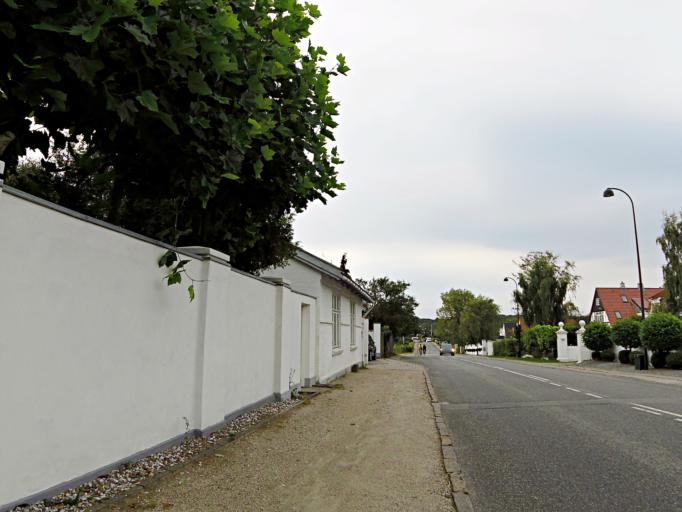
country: DK
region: Capital Region
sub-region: Rudersdal Kommune
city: Trorod
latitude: 55.8149
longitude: 12.5752
